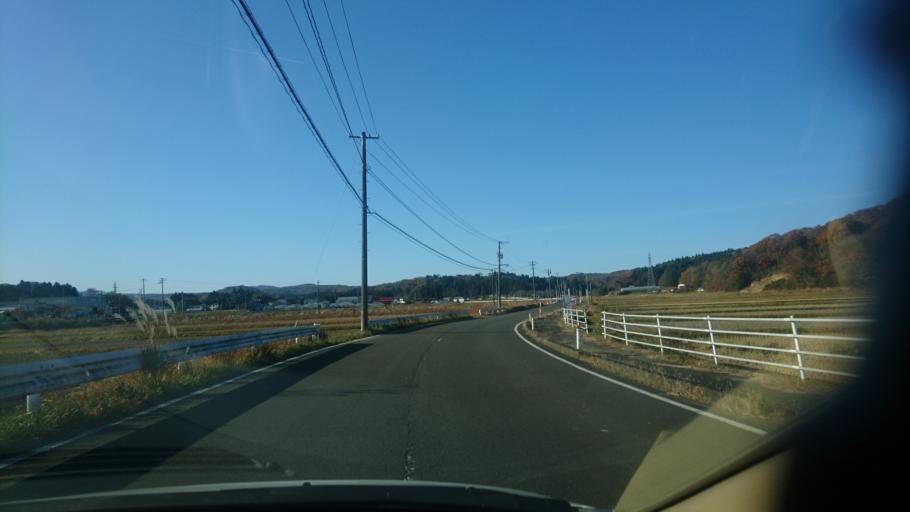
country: JP
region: Miyagi
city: Tomiya
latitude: 38.4748
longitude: 140.8514
